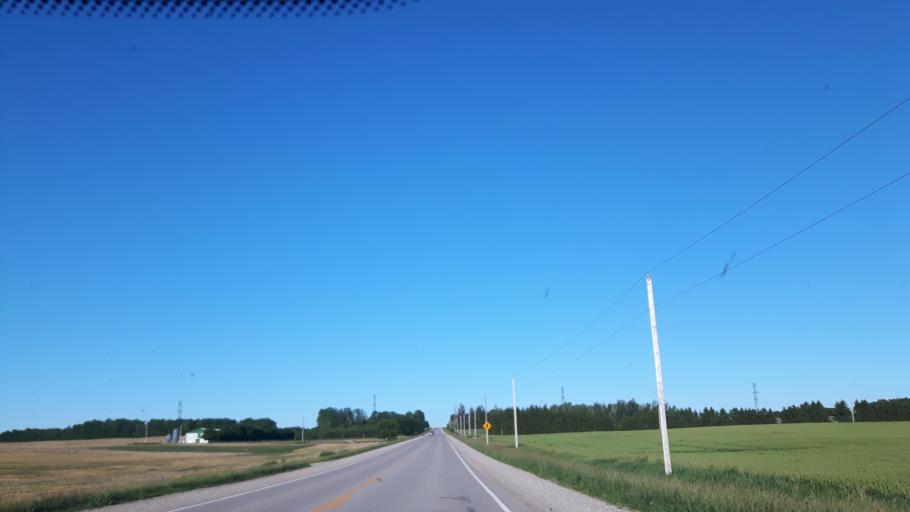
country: CA
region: Ontario
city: Goderich
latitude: 43.6426
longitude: -81.6472
